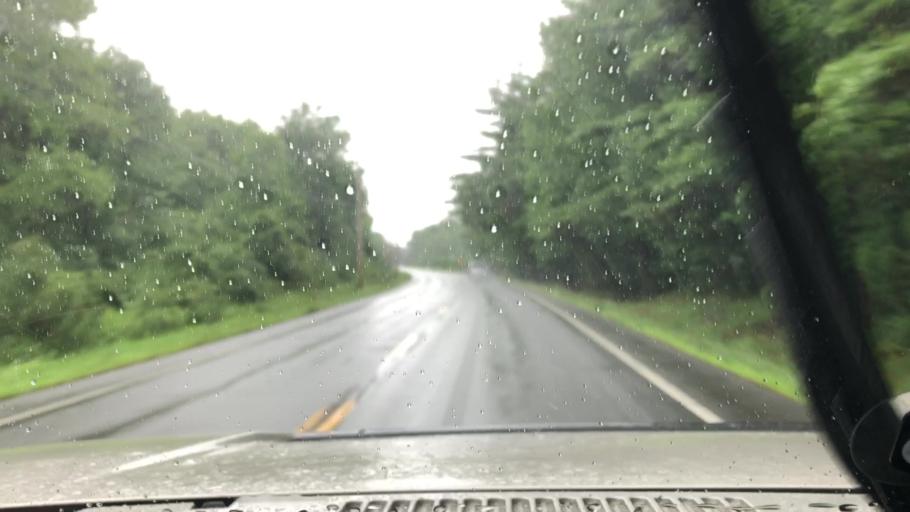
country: US
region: New York
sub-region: Greene County
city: Cairo
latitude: 42.2787
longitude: -73.9797
